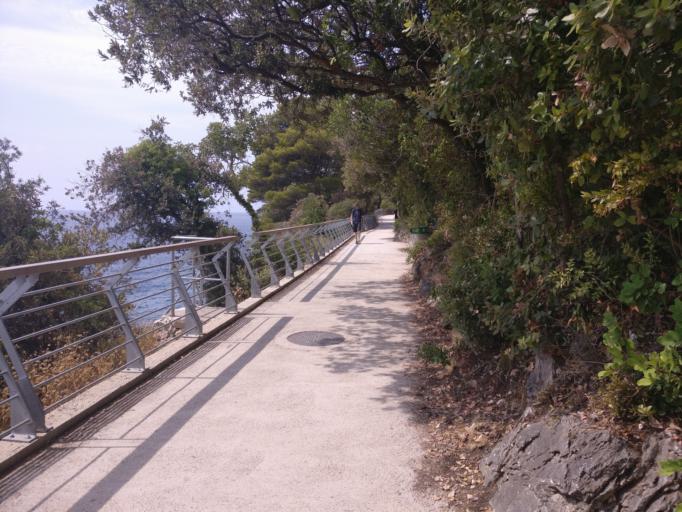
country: HR
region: Dubrovacko-Neretvanska
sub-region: Grad Dubrovnik
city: Dubrovnik
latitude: 42.6572
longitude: 18.0641
